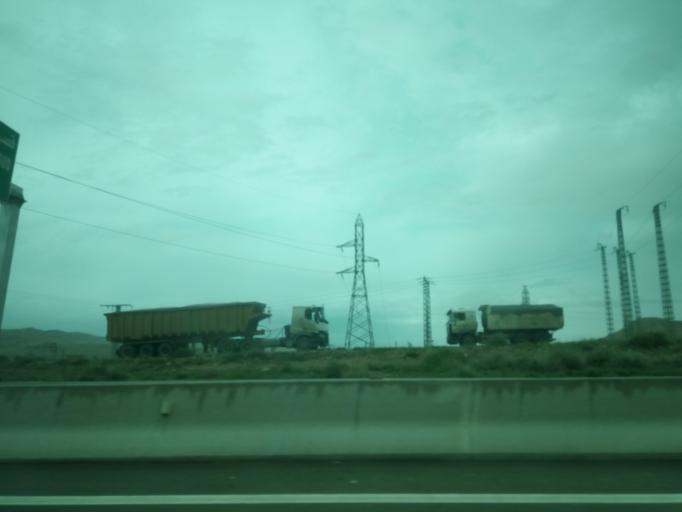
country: DZ
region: Medea
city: Ksar el Boukhari
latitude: 35.8334
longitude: 2.7705
